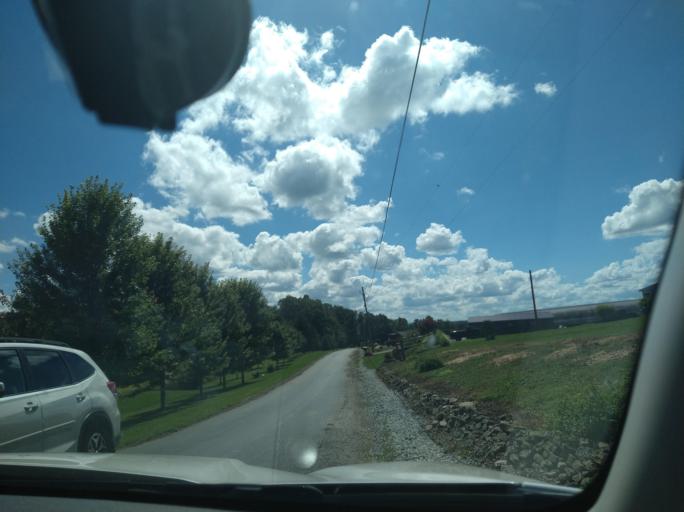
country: US
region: Pennsylvania
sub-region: Fayette County
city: Bear Rocks
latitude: 40.0910
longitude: -79.3665
